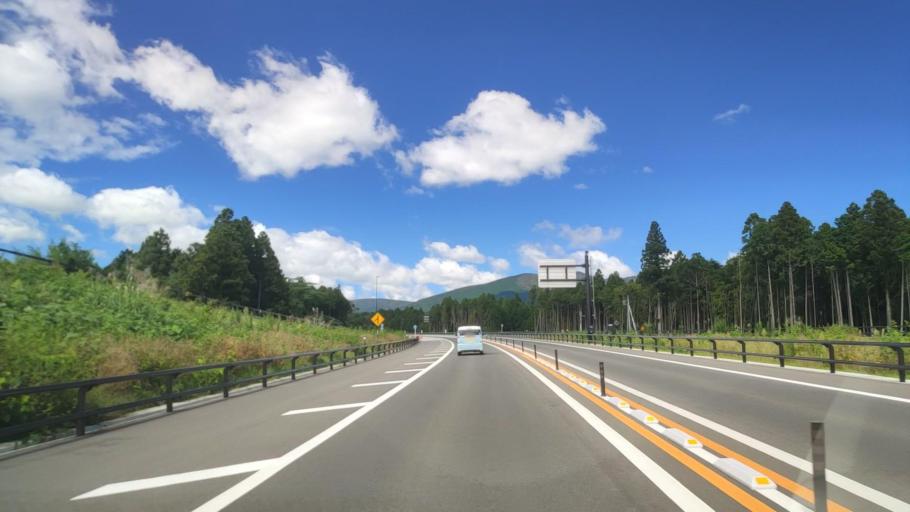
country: JP
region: Shizuoka
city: Gotemba
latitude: 35.3276
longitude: 138.9025
